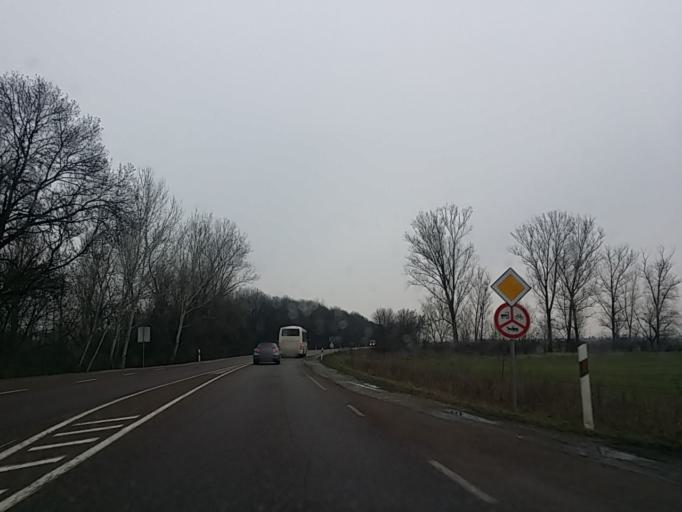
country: HU
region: Borsod-Abauj-Zemplen
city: Mezokeresztes
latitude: 47.8401
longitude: 20.6406
